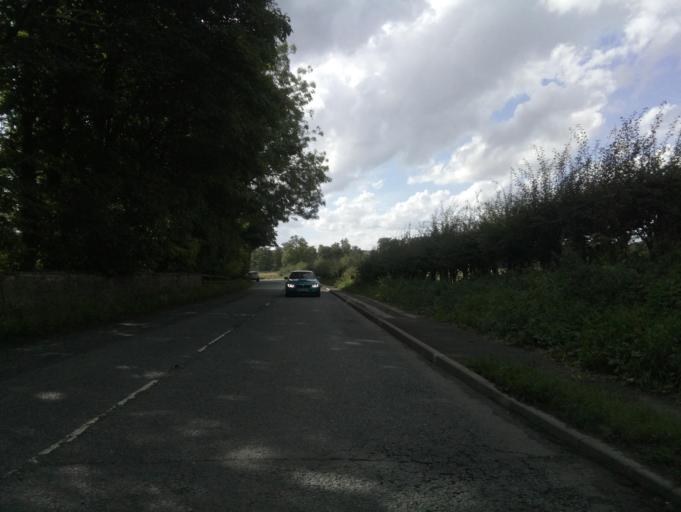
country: GB
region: England
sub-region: North Yorkshire
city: Bedale
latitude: 54.2256
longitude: -1.6500
